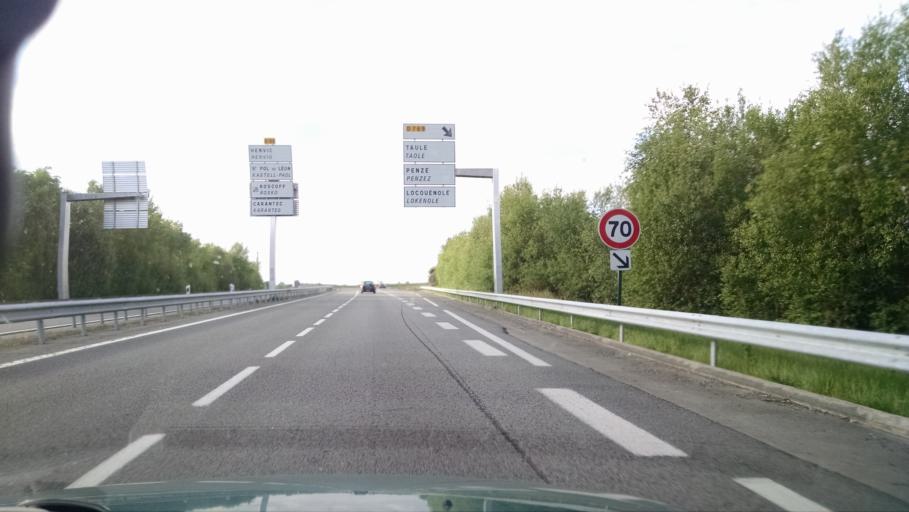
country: FR
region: Brittany
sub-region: Departement du Finistere
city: Taule
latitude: 48.6028
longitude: -3.8866
